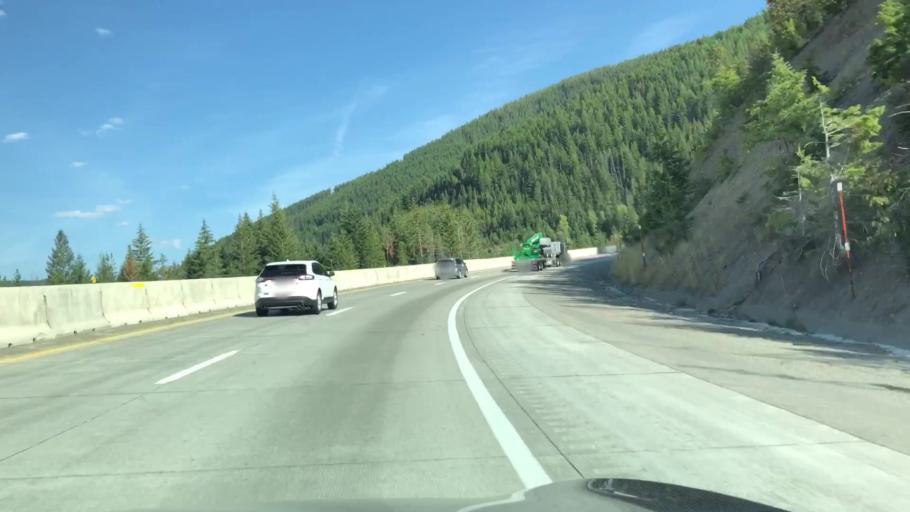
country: US
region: Idaho
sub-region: Shoshone County
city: Wallace
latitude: 47.4611
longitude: -115.7312
